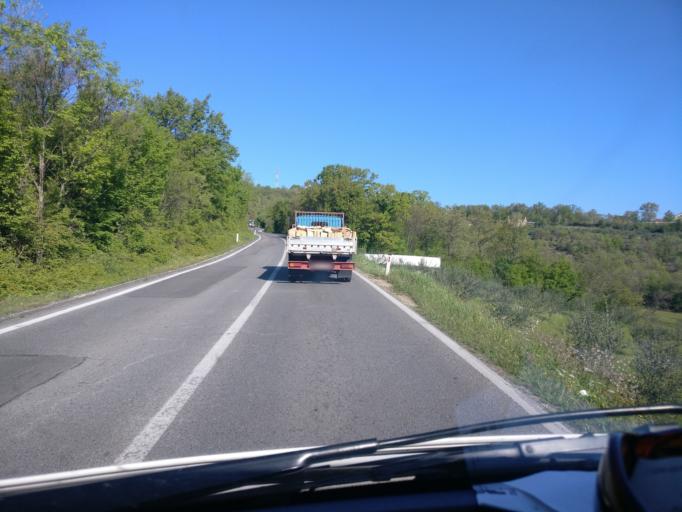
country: BA
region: Federation of Bosnia and Herzegovina
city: Crnici
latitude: 43.1008
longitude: 17.9080
